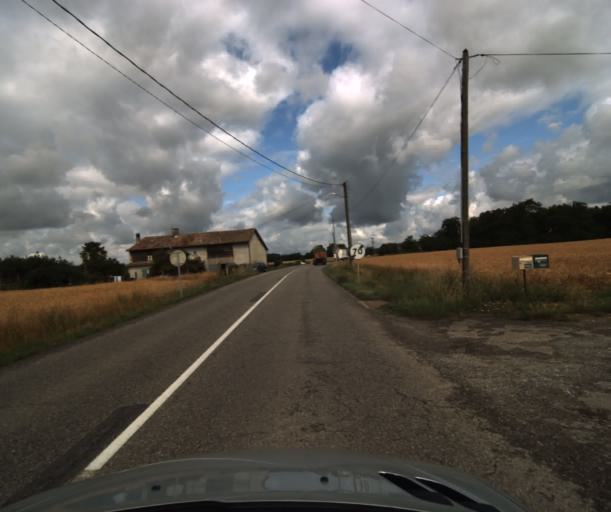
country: FR
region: Midi-Pyrenees
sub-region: Departement du Tarn-et-Garonne
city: Castelsarrasin
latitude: 44.0223
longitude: 1.0649
